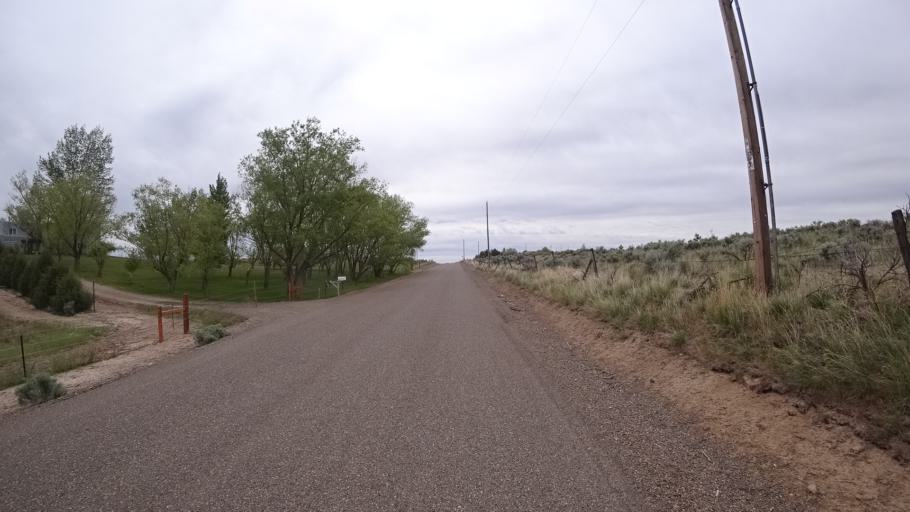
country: US
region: Idaho
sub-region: Ada County
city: Boise
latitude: 43.3863
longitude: -115.9688
